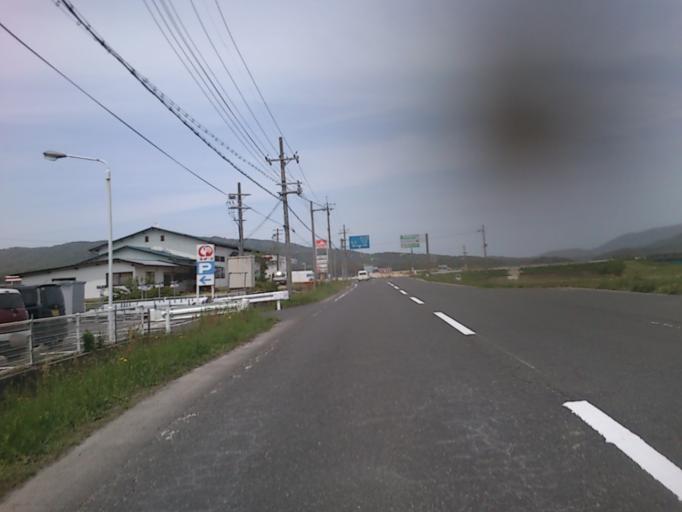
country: JP
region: Kyoto
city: Miyazu
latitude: 35.6687
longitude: 135.0866
